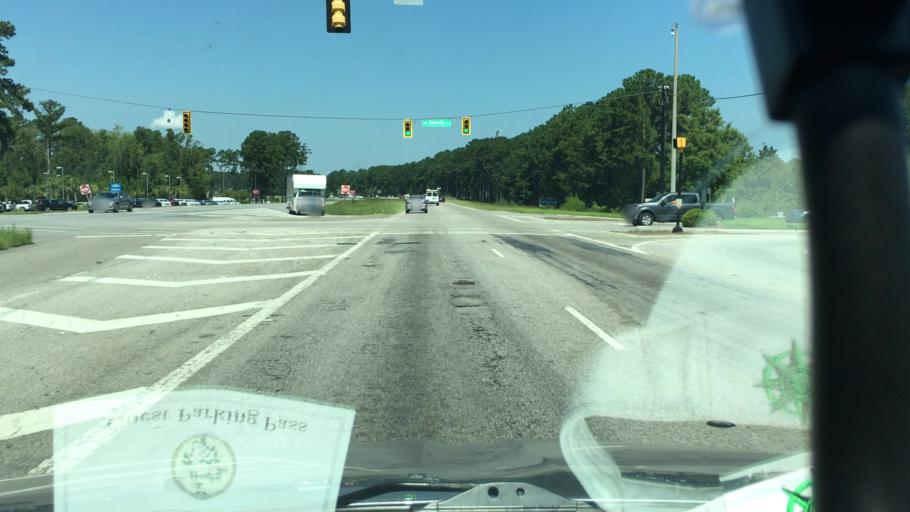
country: US
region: South Carolina
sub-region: Jasper County
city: Hardeeville
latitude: 32.3079
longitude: -80.9762
